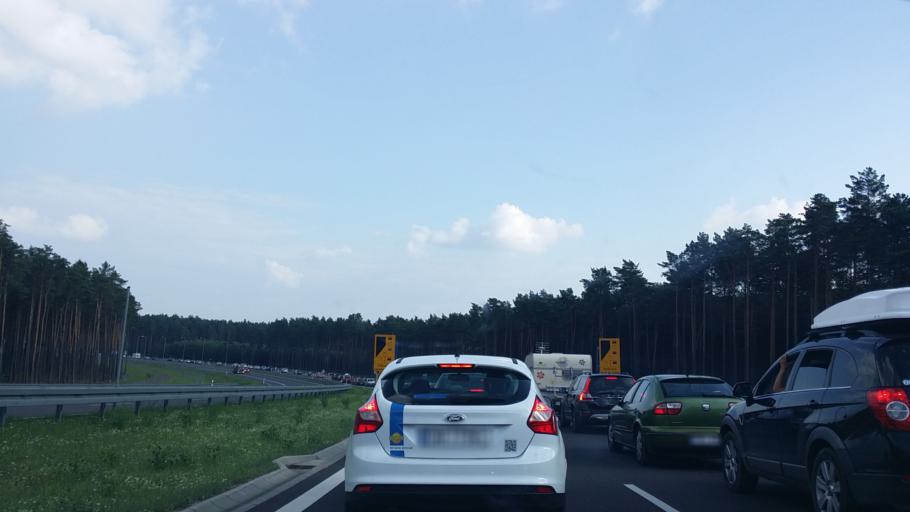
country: PL
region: Lubusz
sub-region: Powiat miedzyrzecki
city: Miedzyrzecz
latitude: 52.4755
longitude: 15.5531
